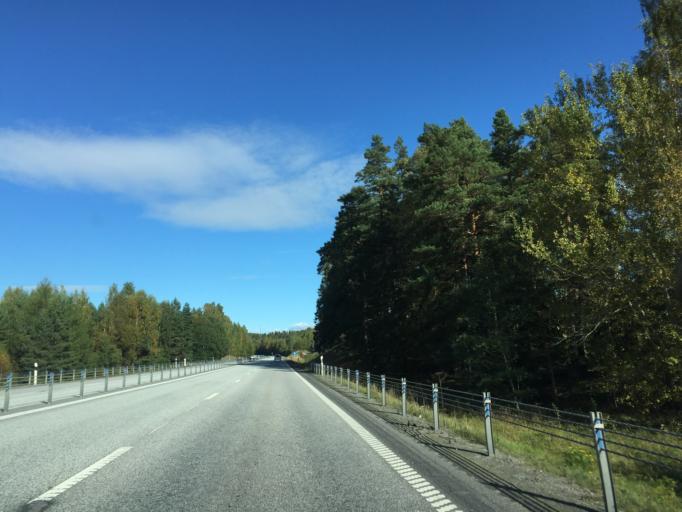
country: SE
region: OErebro
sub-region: Orebro Kommun
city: Hovsta
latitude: 59.3353
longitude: 15.2350
